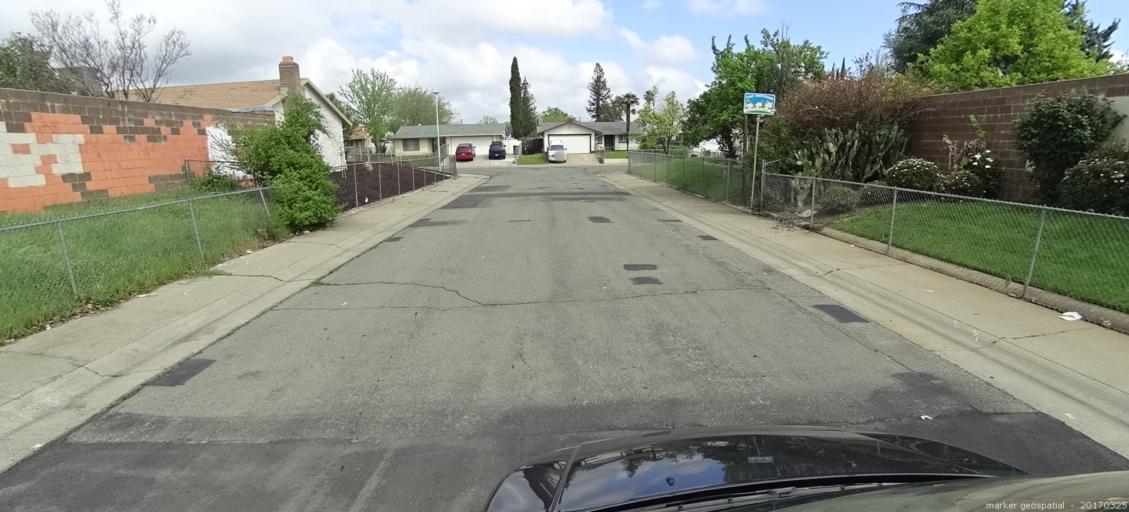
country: US
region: California
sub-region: Sacramento County
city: Florin
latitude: 38.5162
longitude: -121.4258
